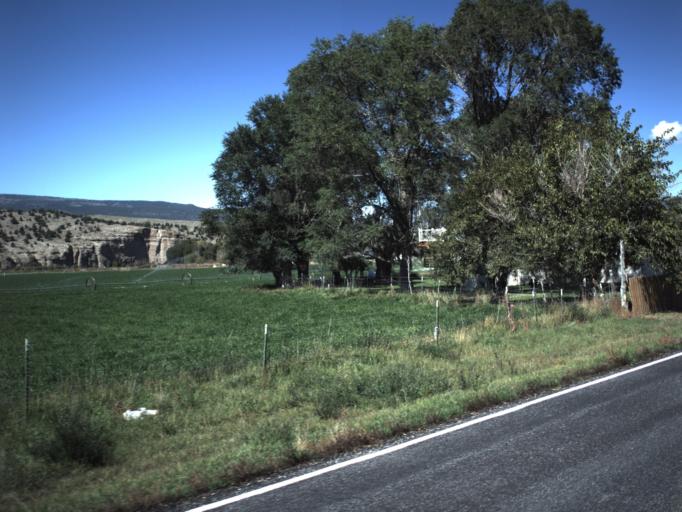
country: US
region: Utah
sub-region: Piute County
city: Junction
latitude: 38.0890
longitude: -111.9813
